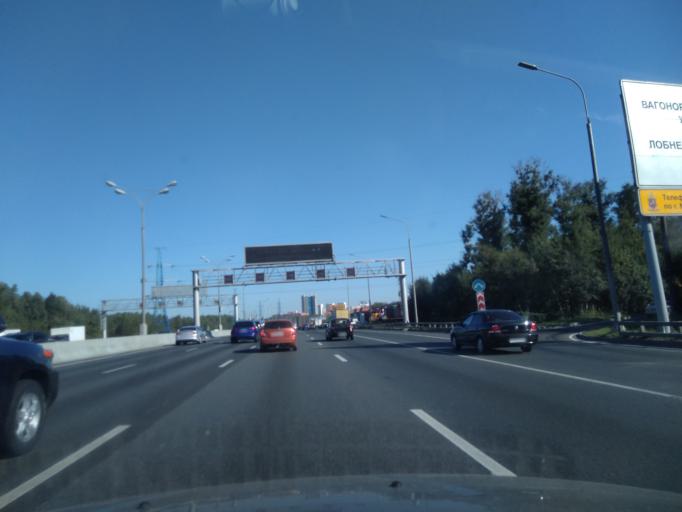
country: RU
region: Moscow
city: Businovo
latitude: 55.9018
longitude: 37.5189
